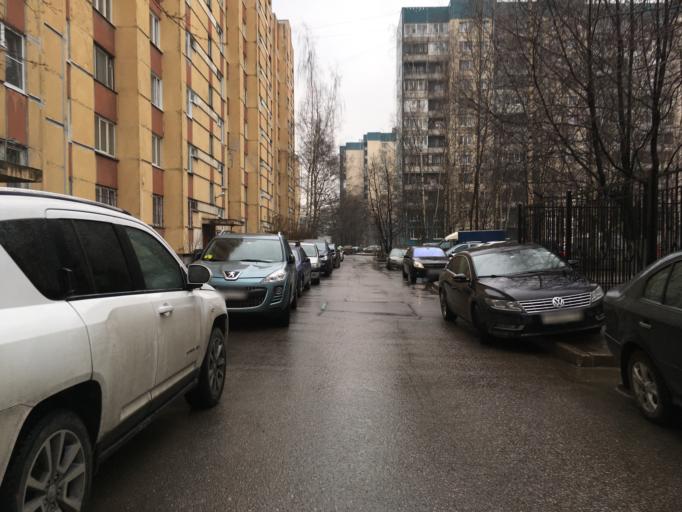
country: RU
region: St.-Petersburg
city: Komendantsky aerodrom
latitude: 60.0129
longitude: 30.2611
